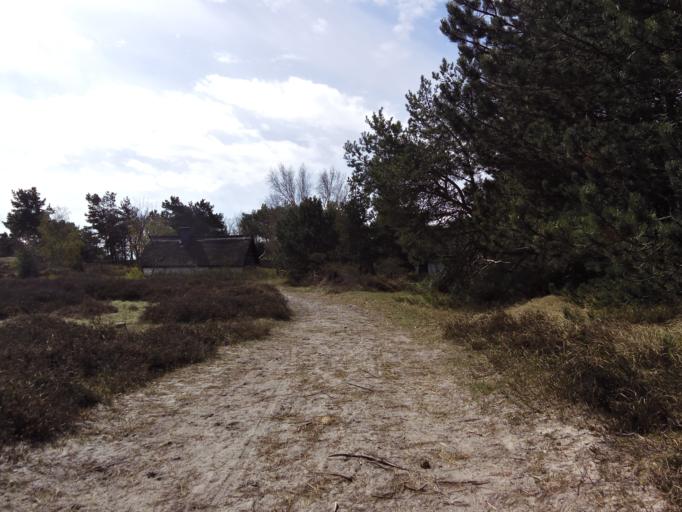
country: DE
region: Mecklenburg-Vorpommern
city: Hiddensee
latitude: 54.5465
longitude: 13.0945
